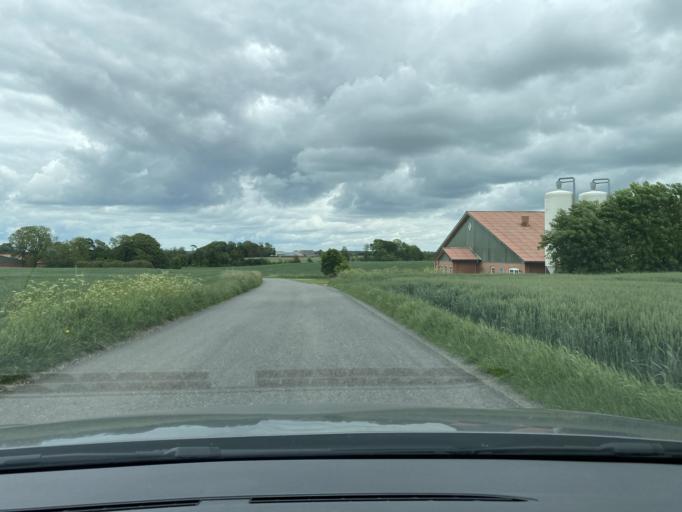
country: DK
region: South Denmark
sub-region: Vejle Kommune
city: Vejle
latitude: 55.6607
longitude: 9.4772
